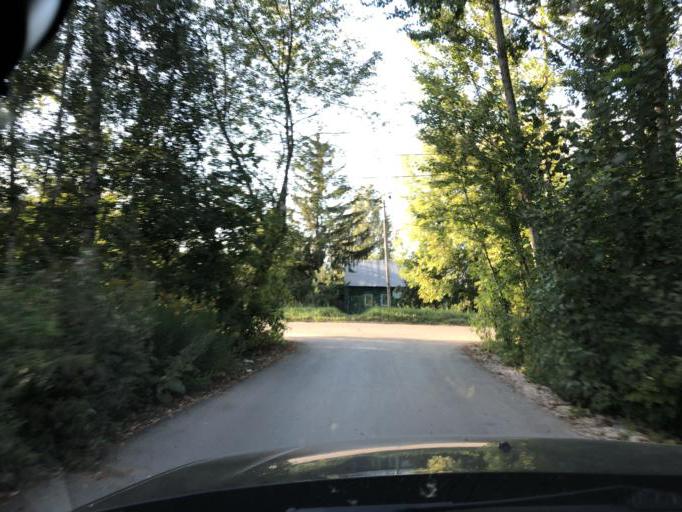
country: RU
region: Tula
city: Kosaya Gora
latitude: 54.1780
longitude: 37.5435
